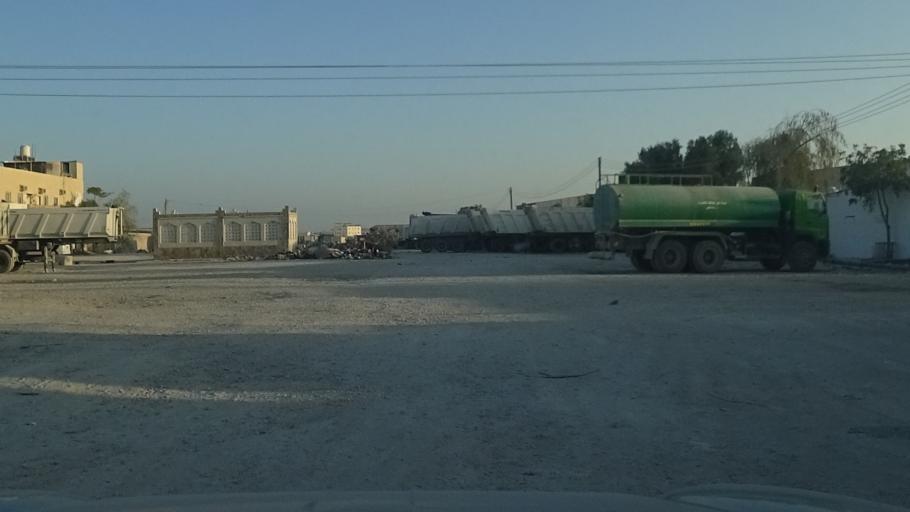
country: OM
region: Zufar
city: Salalah
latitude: 17.0301
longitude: 54.0415
